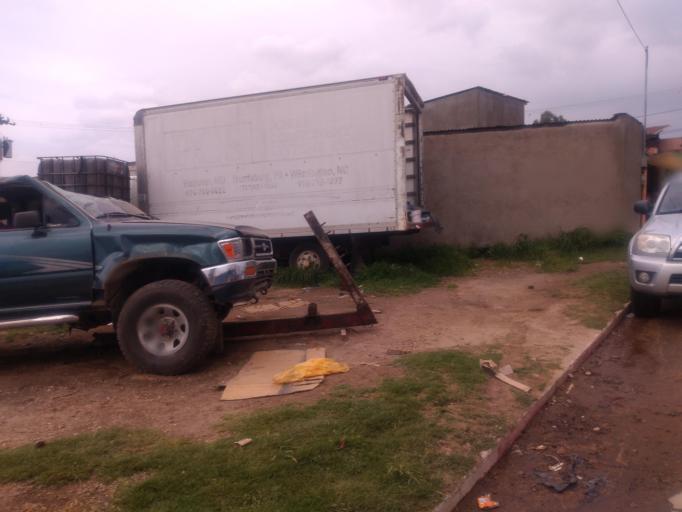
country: GT
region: Quetzaltenango
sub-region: Municipio de La Esperanza
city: La Esperanza
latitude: 14.8647
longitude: -91.5722
